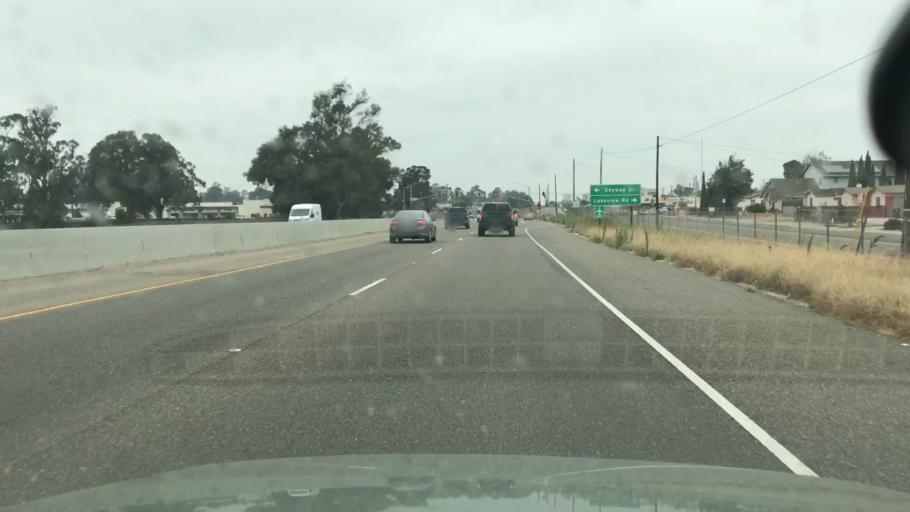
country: US
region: California
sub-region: Santa Barbara County
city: Orcutt
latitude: 34.8924
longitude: -120.4364
